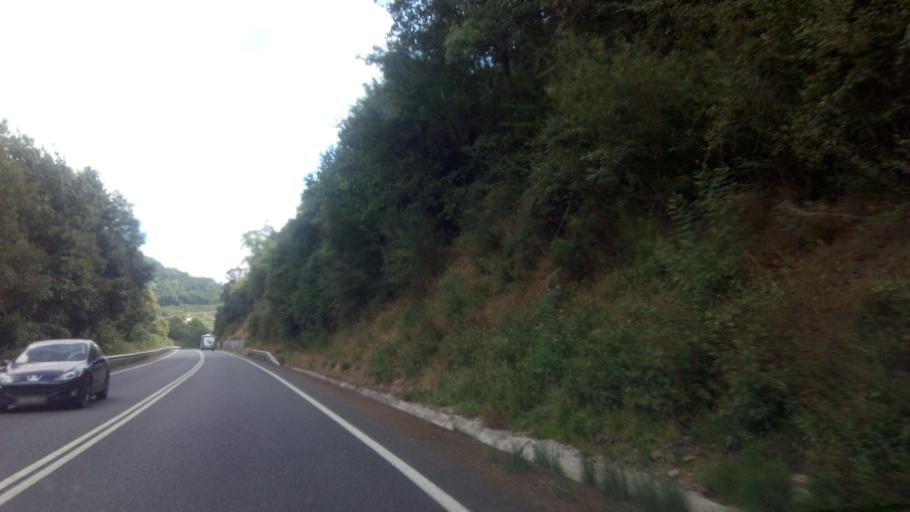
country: ES
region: Galicia
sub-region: Provincia de Ourense
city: Nogueira de Ramuin
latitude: 42.4119
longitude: -7.7829
